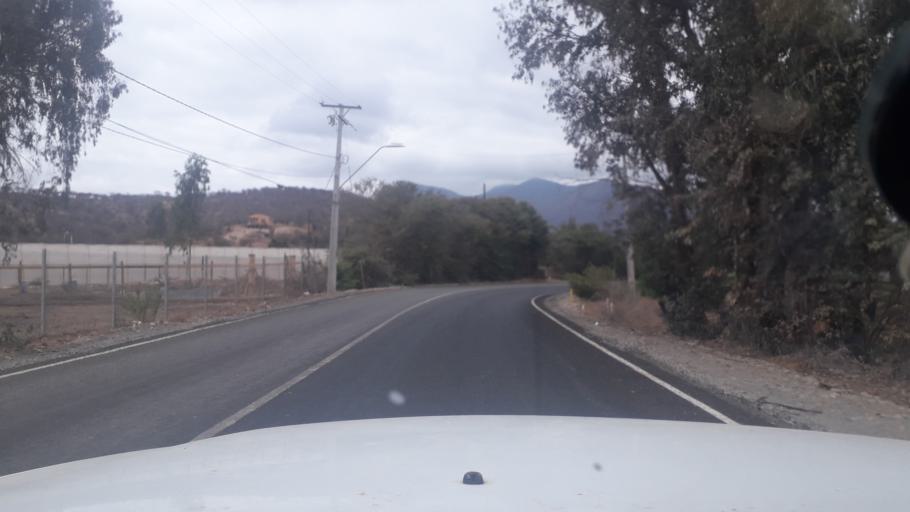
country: CL
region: Valparaiso
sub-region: Provincia de Marga Marga
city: Limache
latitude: -33.0265
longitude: -71.2747
